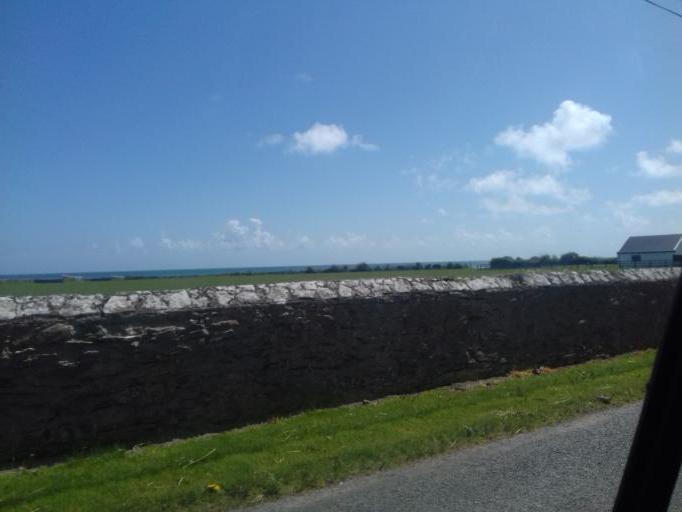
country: IE
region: Munster
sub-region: Waterford
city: Dunmore East
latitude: 52.1506
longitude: -6.9022
